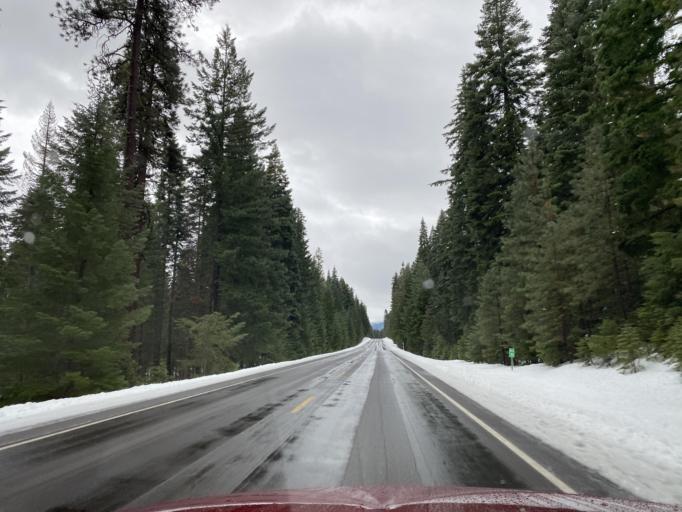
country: US
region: Oregon
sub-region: Klamath County
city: Klamath Falls
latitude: 42.5174
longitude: -122.0839
